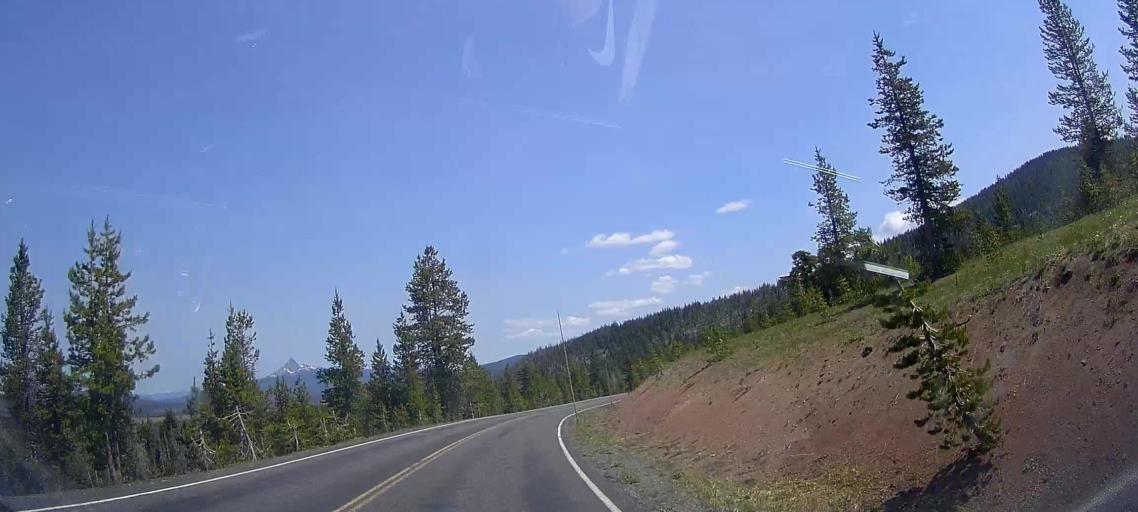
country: US
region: Oregon
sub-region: Jackson County
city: Shady Cove
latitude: 42.9920
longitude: -122.1424
